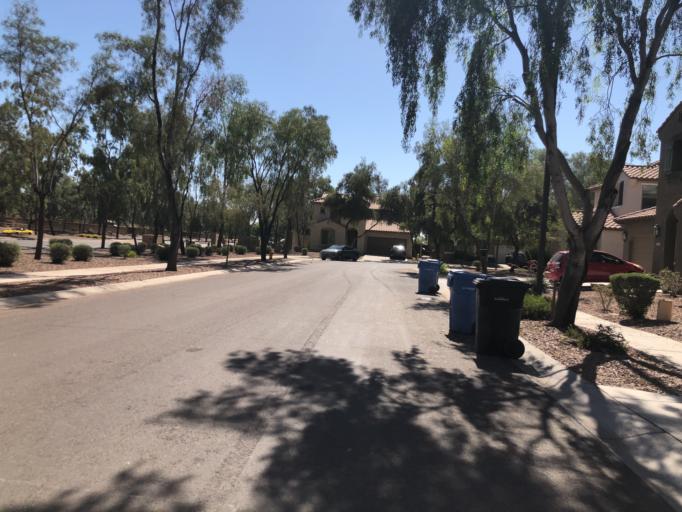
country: US
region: Arizona
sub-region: Maricopa County
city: Queen Creek
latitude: 33.2774
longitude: -111.7084
